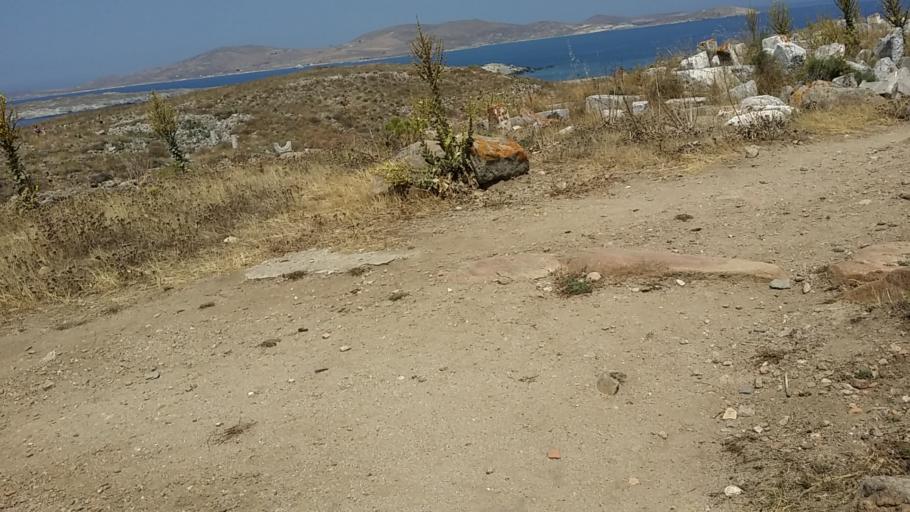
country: GR
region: South Aegean
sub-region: Nomos Kykladon
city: Mykonos
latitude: 37.3967
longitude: 25.2710
